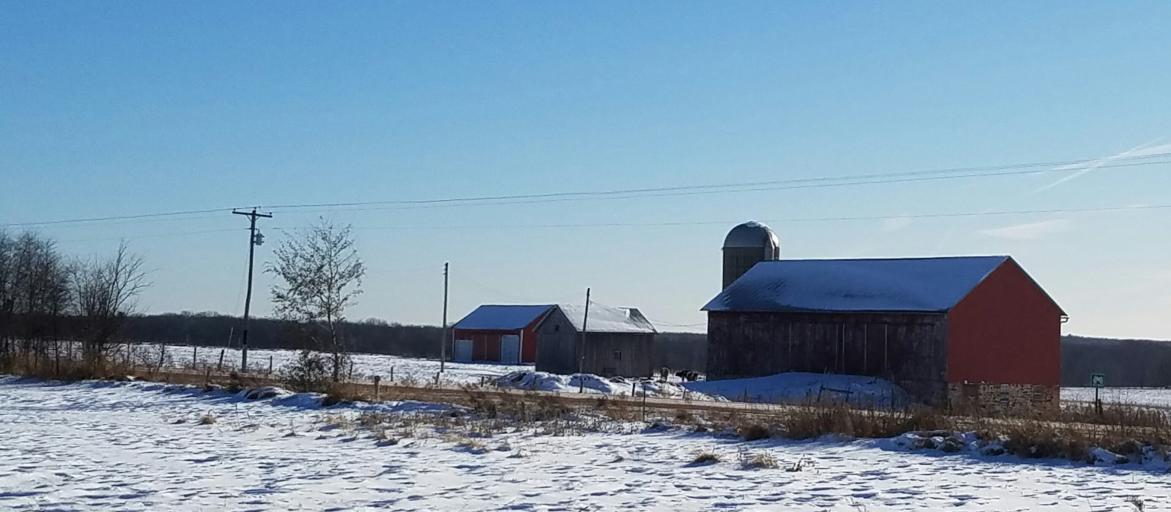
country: US
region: Wisconsin
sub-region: Clark County
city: Neillsville
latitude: 44.5680
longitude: -90.4360
